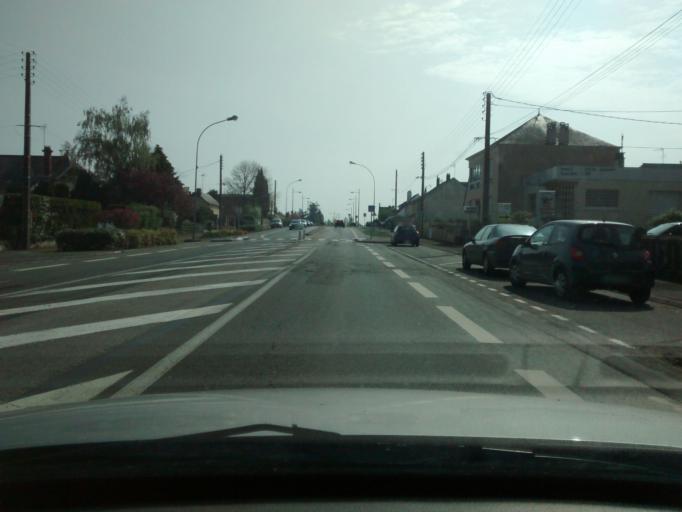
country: FR
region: Pays de la Loire
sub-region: Departement de la Mayenne
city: Saint-Berthevin
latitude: 48.0692
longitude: -0.8261
